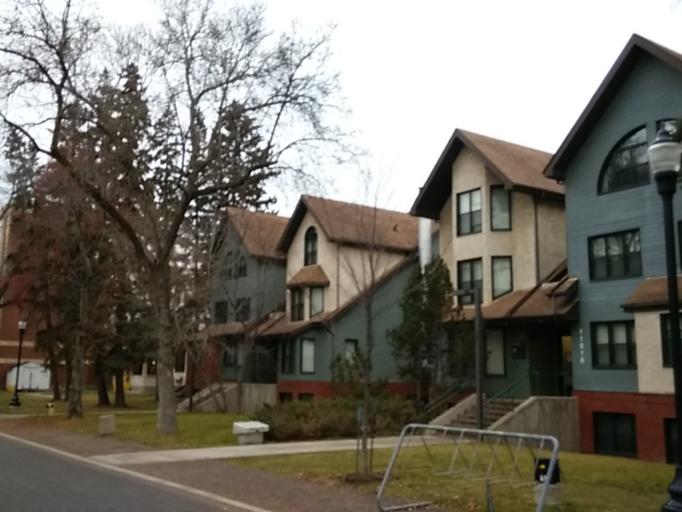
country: CA
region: Alberta
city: Edmonton
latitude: 53.5238
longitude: -113.5158
